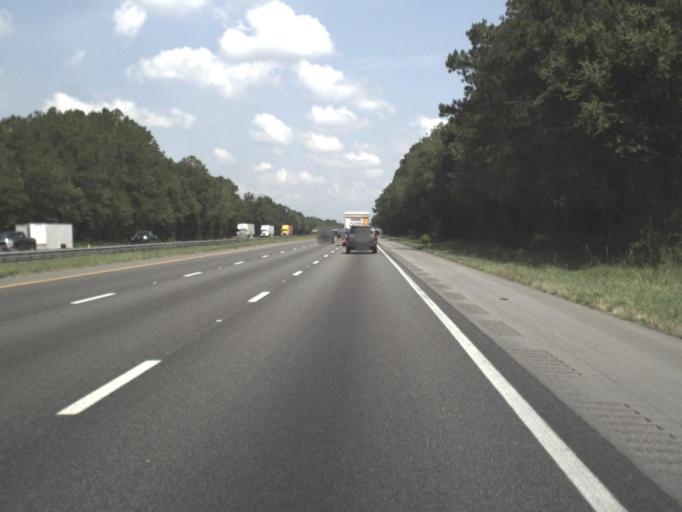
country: US
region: Georgia
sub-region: Echols County
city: Statenville
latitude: 30.5665
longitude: -83.0919
